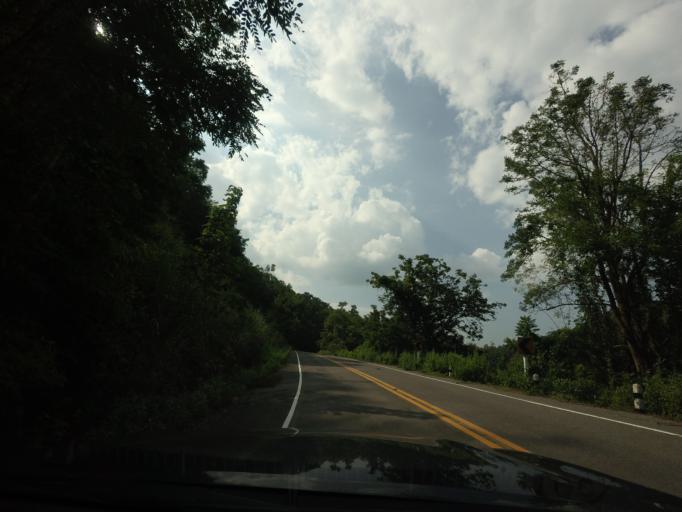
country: TH
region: Nan
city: Na Noi
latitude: 18.2846
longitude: 100.9355
